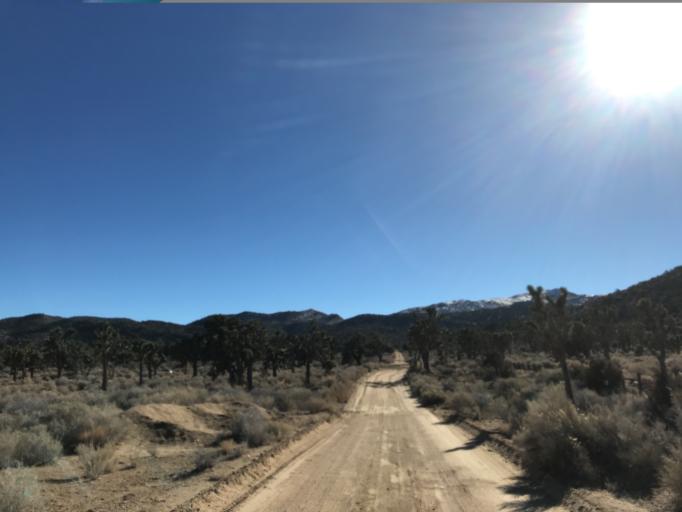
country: US
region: California
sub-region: San Bernardino County
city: Morongo Valley
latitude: 34.2282
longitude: -116.6389
